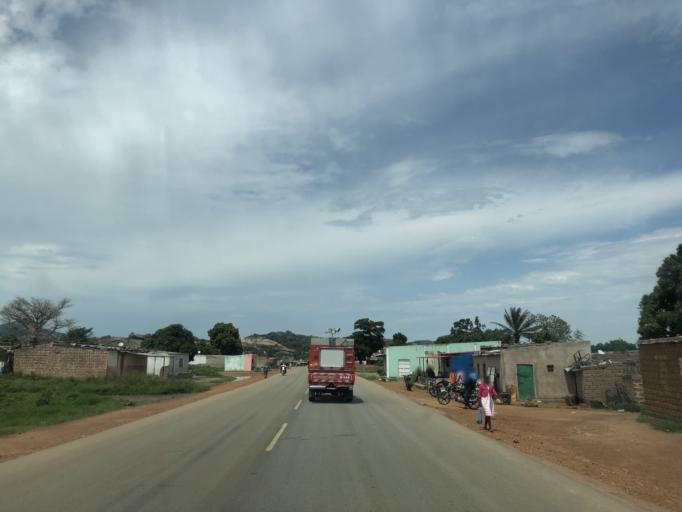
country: AO
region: Cuanza Sul
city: Quibala
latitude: -10.7360
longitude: 14.9913
